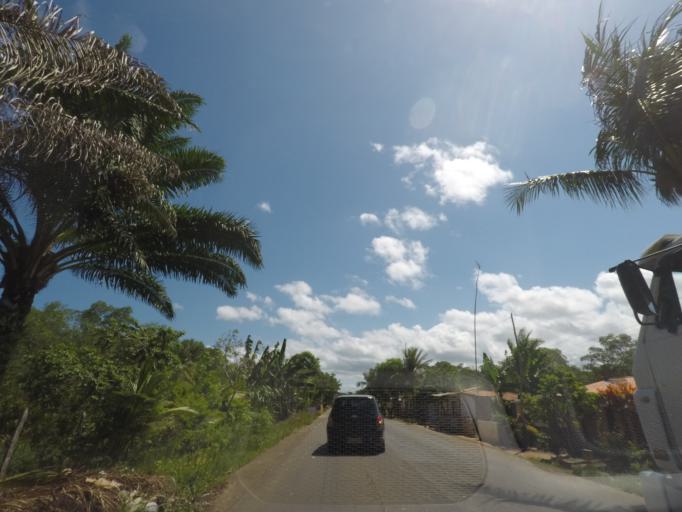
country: BR
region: Bahia
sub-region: Taperoa
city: Taperoa
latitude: -13.4780
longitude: -39.0900
